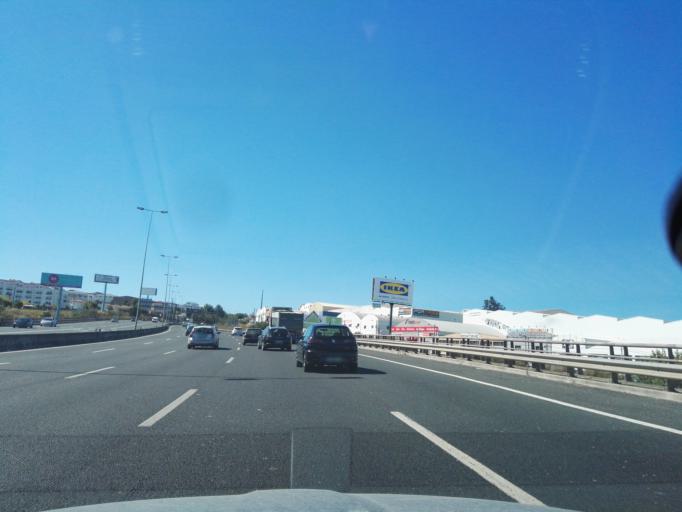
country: PT
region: Lisbon
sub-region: Loures
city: Sacavem
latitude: 38.7952
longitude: -9.1179
